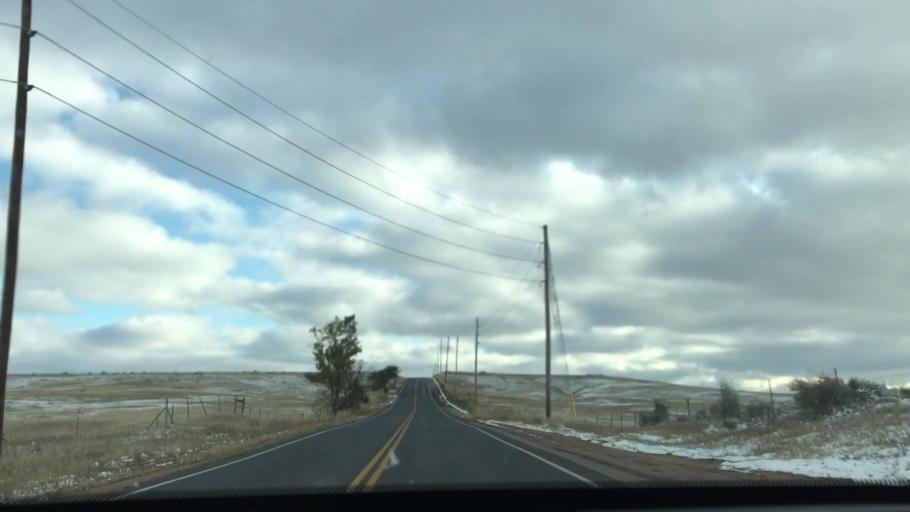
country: US
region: Colorado
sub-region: Boulder County
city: Lafayette
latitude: 39.9641
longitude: -105.0723
